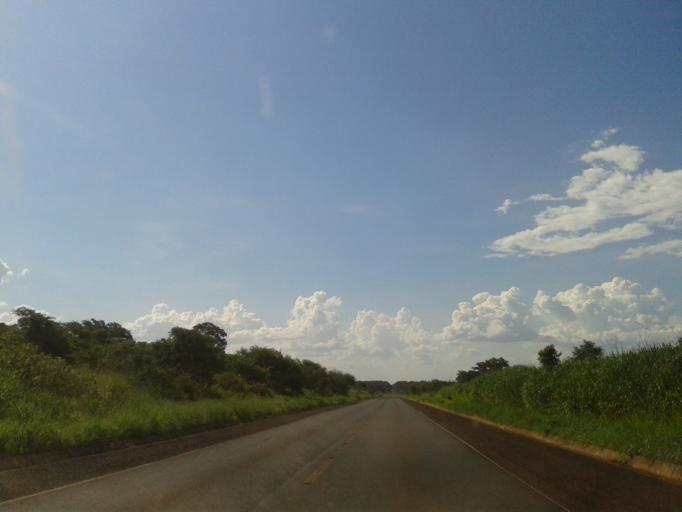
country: BR
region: Minas Gerais
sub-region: Santa Vitoria
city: Santa Vitoria
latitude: -19.0461
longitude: -50.4066
